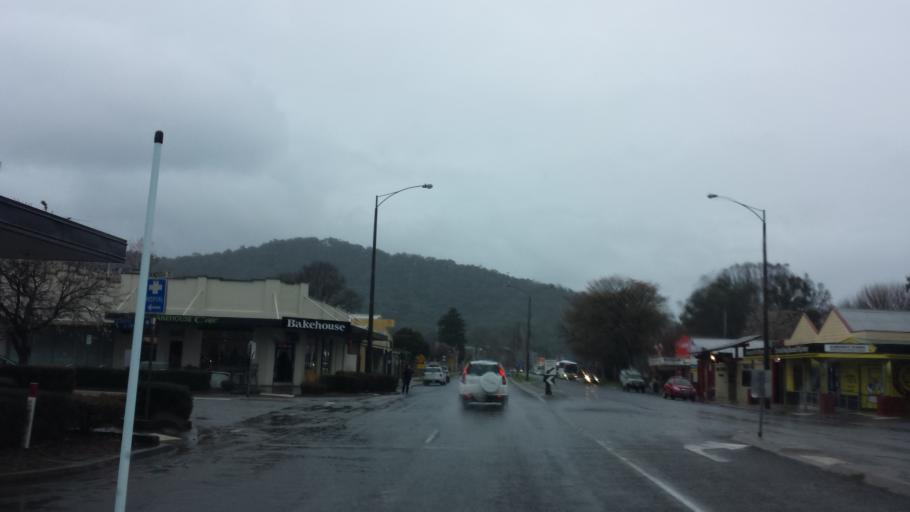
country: AU
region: Victoria
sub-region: Wangaratta
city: Wangaratta
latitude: -36.5606
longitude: 146.7236
